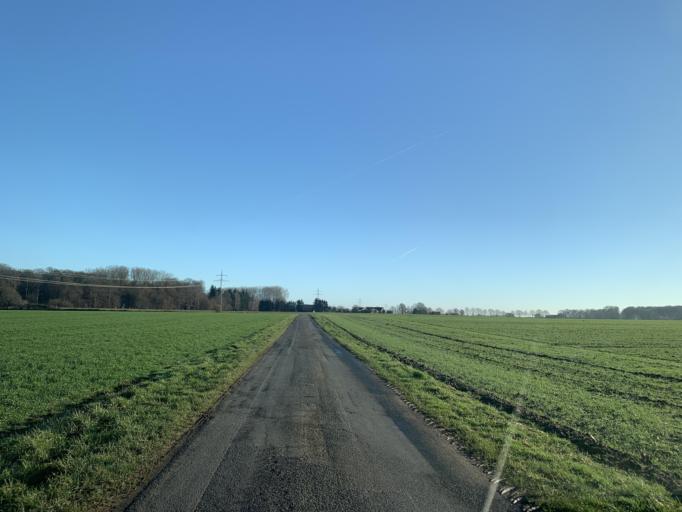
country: DE
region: North Rhine-Westphalia
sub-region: Regierungsbezirk Munster
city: Dulmen
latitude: 51.8710
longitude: 7.2806
